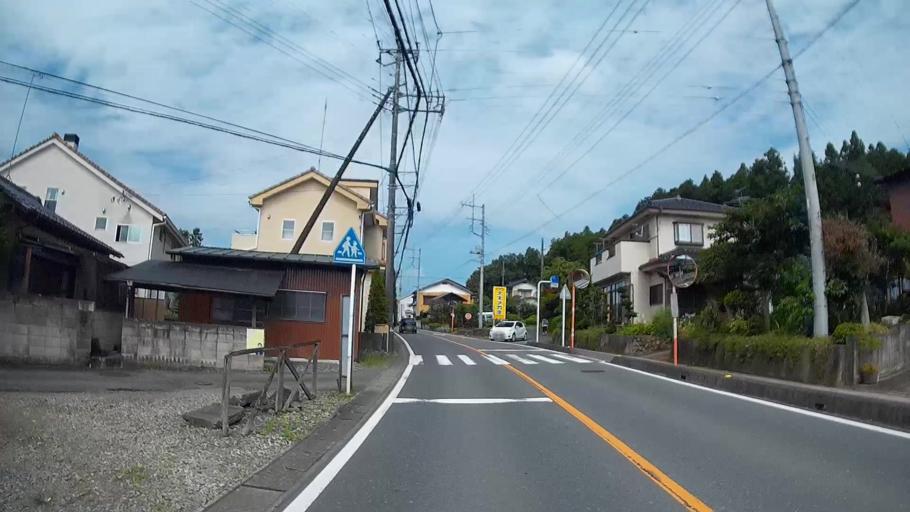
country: JP
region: Saitama
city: Hanno
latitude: 35.8597
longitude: 139.2984
